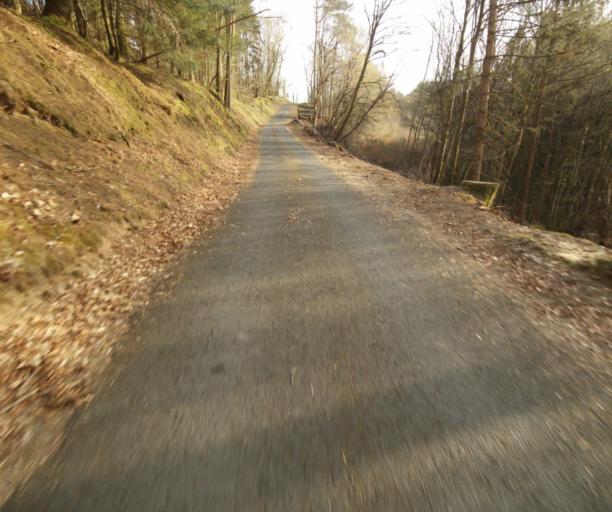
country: FR
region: Limousin
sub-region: Departement de la Correze
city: Correze
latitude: 45.3519
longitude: 1.8238
